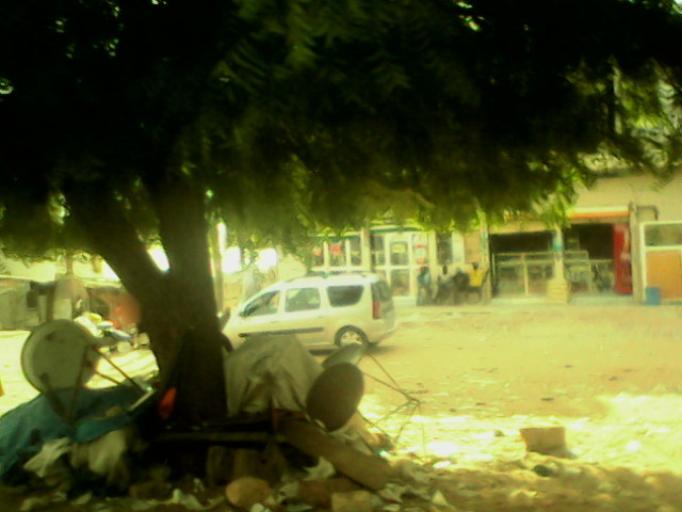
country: SN
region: Diourbel
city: Touba
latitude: 14.8651
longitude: -15.8971
